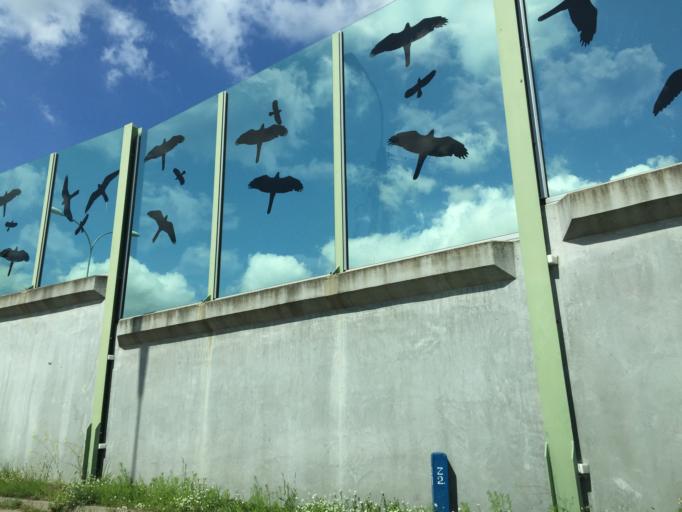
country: PL
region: Podlasie
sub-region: Bialystok
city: Bialystok
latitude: 53.1192
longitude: 23.1718
